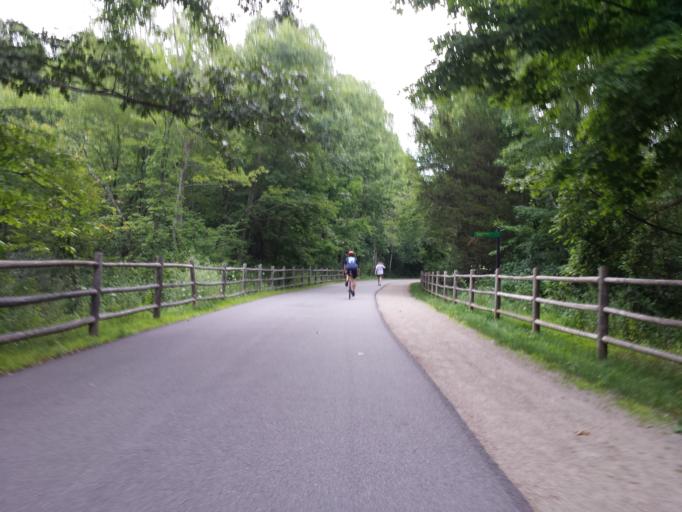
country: US
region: New York
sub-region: Dutchess County
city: Hillside Lake
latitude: 41.5864
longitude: -73.8101
